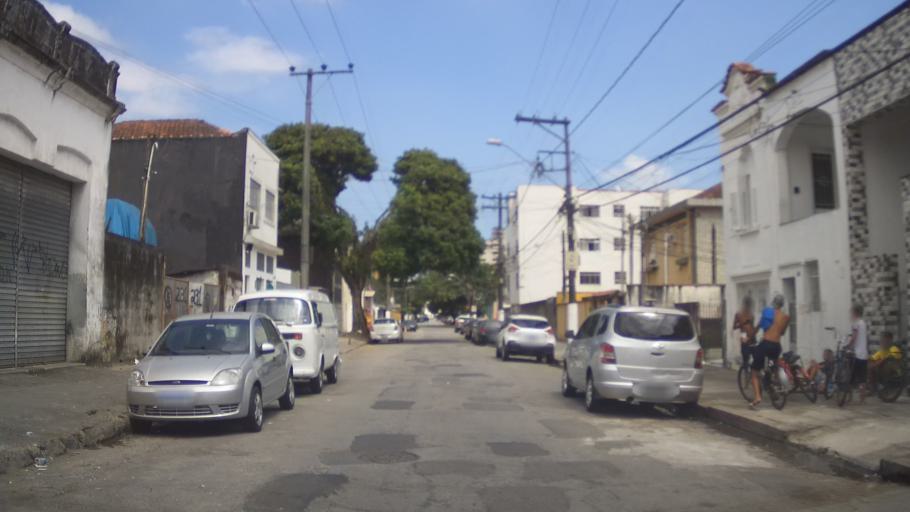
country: BR
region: Sao Paulo
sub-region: Santos
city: Santos
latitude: -23.9592
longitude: -46.3123
